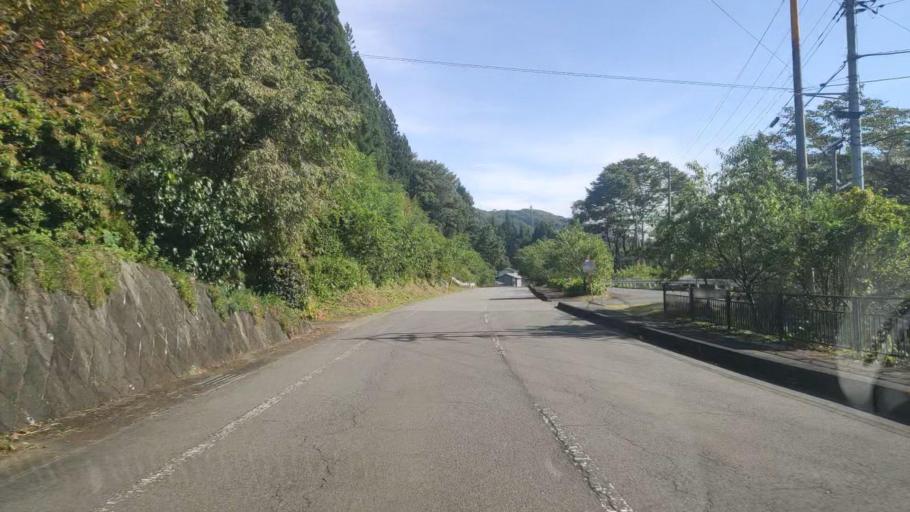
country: JP
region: Gunma
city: Nakanojomachi
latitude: 36.6062
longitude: 138.7201
